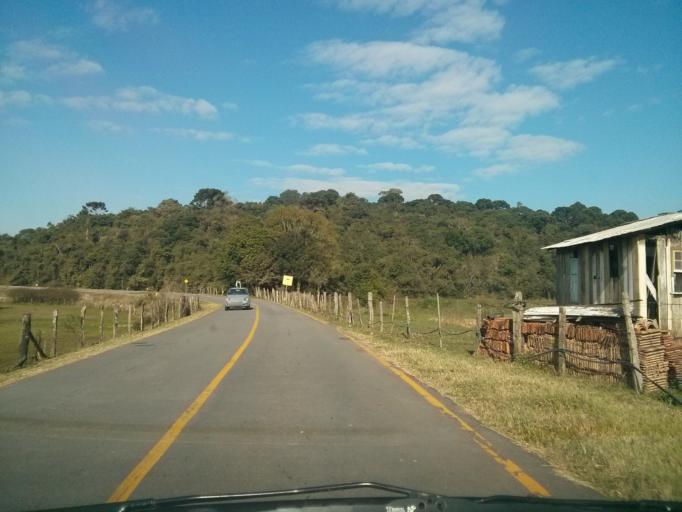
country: BR
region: Parana
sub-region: Sao Jose Dos Pinhais
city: Sao Jose dos Pinhais
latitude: -25.5528
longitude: -49.2264
